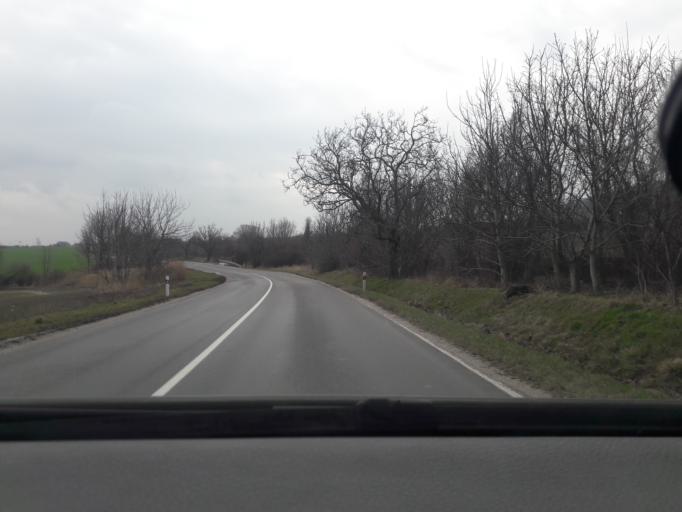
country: SK
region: Trnavsky
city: Smolenice
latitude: 48.4539
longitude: 17.4266
